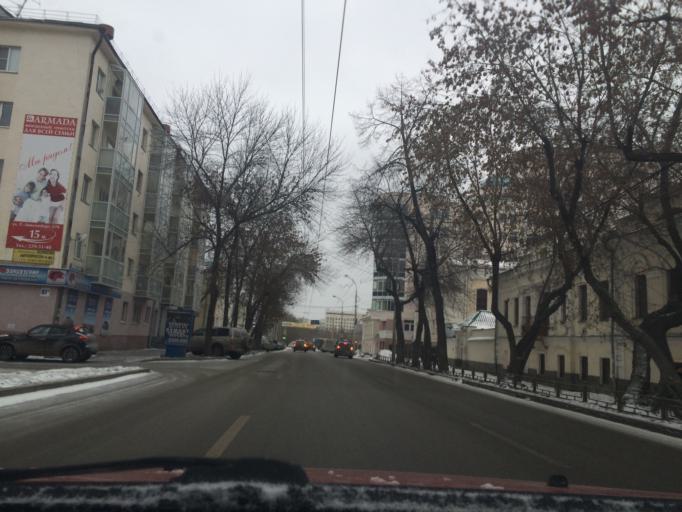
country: RU
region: Sverdlovsk
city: Yekaterinburg
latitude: 56.8253
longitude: 60.6141
